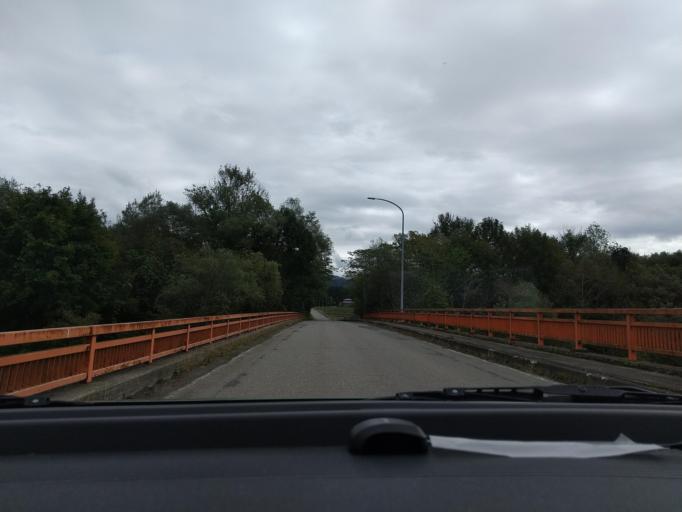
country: JP
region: Akita
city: Kakunodatemachi
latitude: 39.5924
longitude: 140.5939
